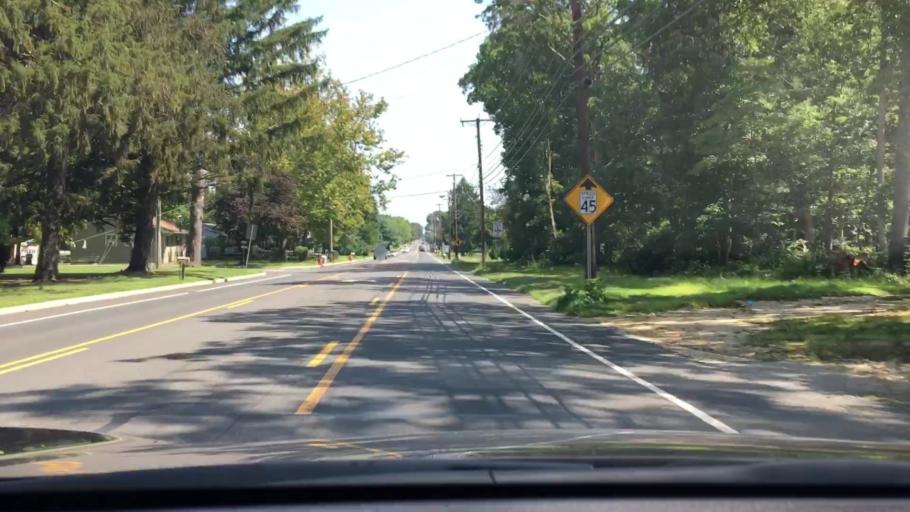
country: US
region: New Jersey
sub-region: Cumberland County
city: Millville
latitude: 39.3798
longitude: -75.0723
